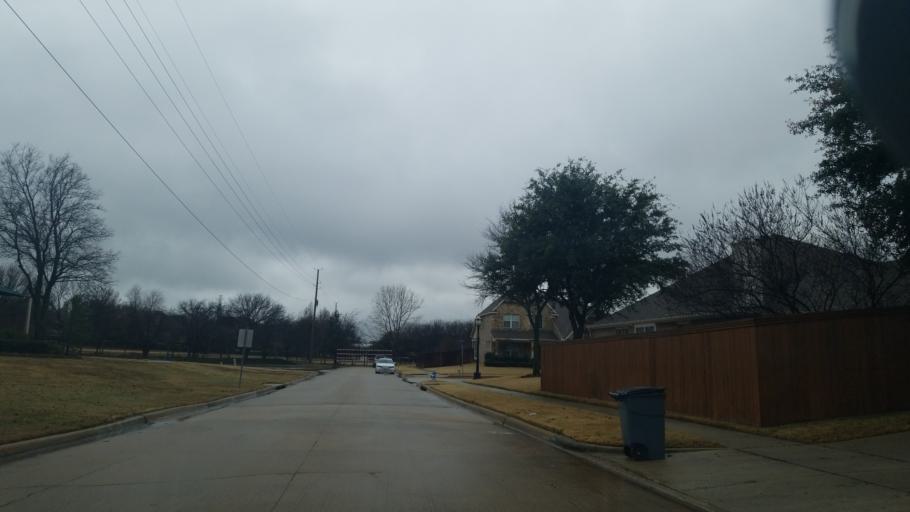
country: US
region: Texas
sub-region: Denton County
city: Corinth
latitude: 33.1527
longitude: -97.0805
